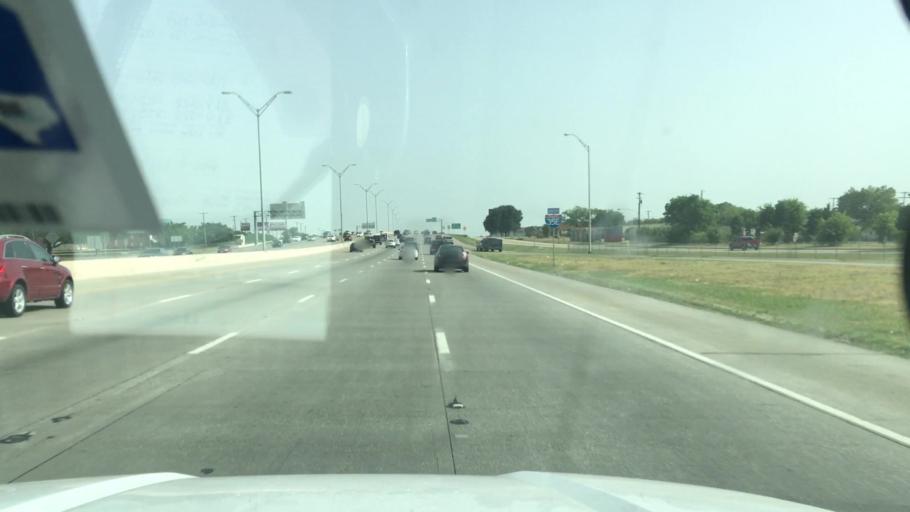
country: US
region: Texas
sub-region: Dallas County
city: DeSoto
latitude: 32.6383
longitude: -96.8234
